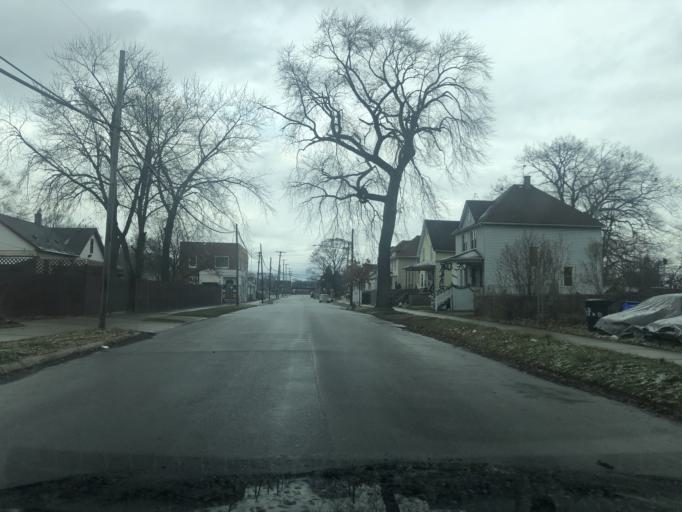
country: US
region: Michigan
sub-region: Wayne County
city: River Rouge
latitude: 42.3080
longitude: -83.1140
